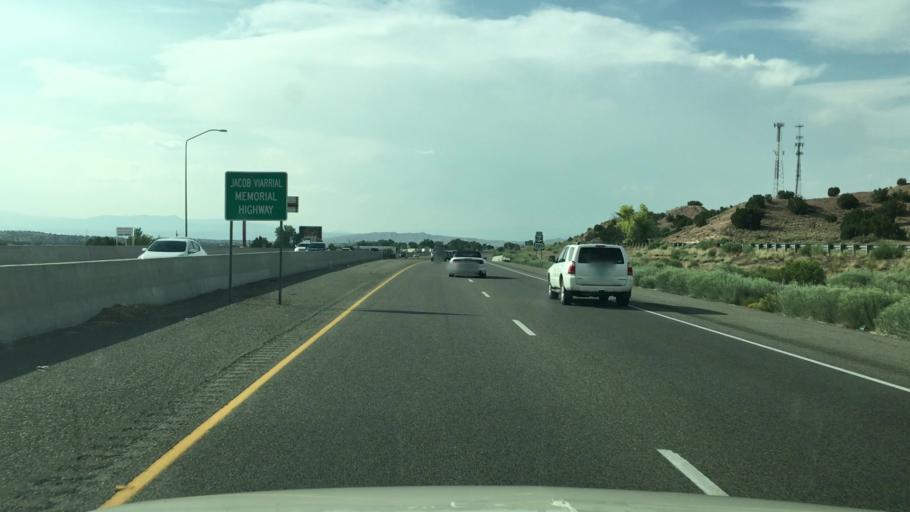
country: US
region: New Mexico
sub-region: Santa Fe County
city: Nambe
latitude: 35.8434
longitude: -105.9916
